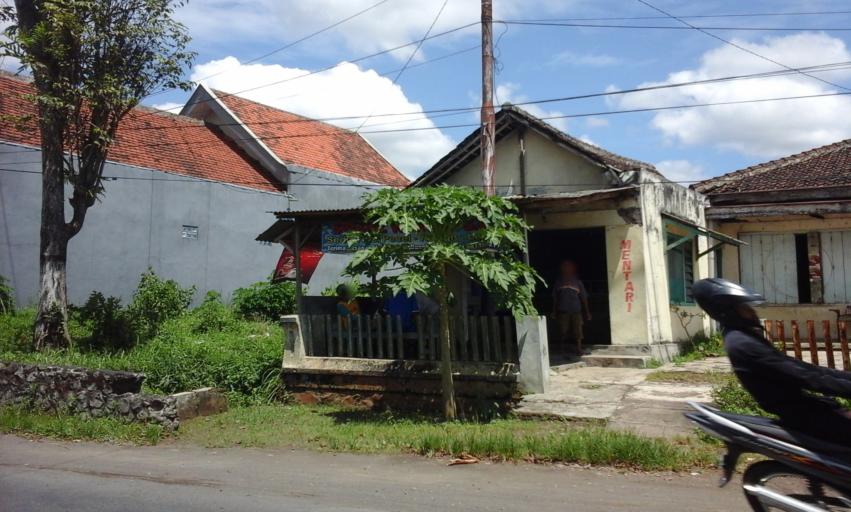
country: ID
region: East Java
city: Sumberketangi
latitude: -8.1860
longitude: 113.7380
